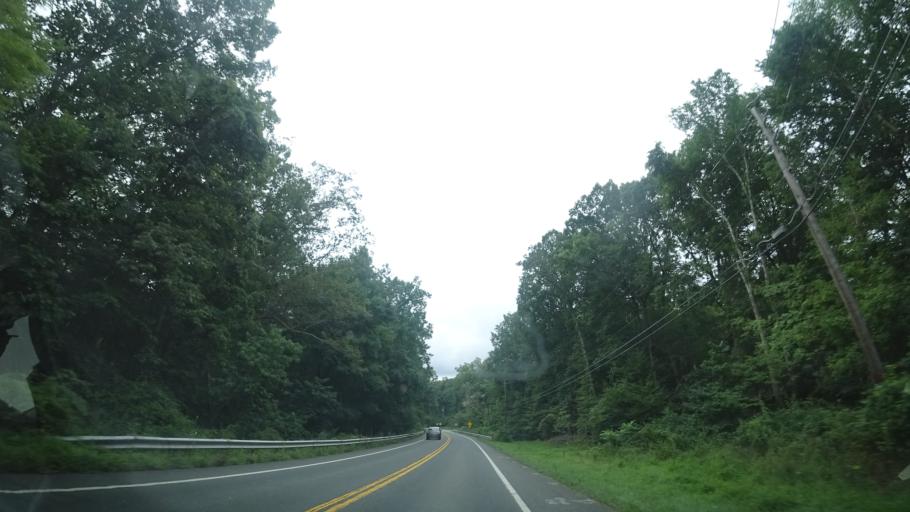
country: US
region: Maryland
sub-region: Montgomery County
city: Darnestown
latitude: 39.0671
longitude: -77.3058
